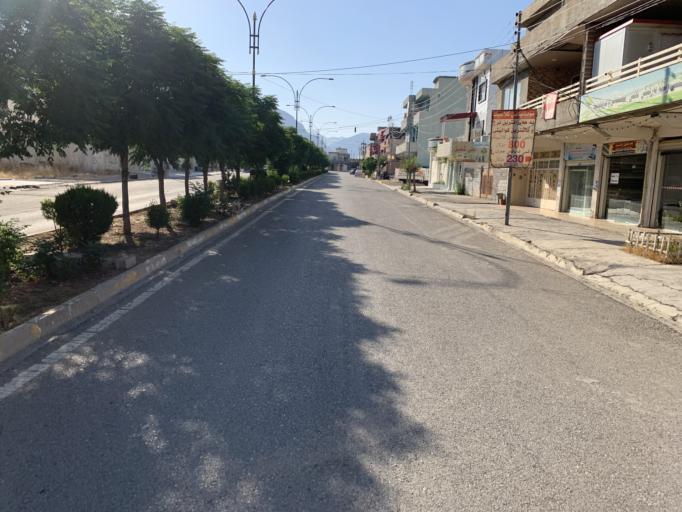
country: IQ
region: As Sulaymaniyah
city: Raniye
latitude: 36.2415
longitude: 44.8743
